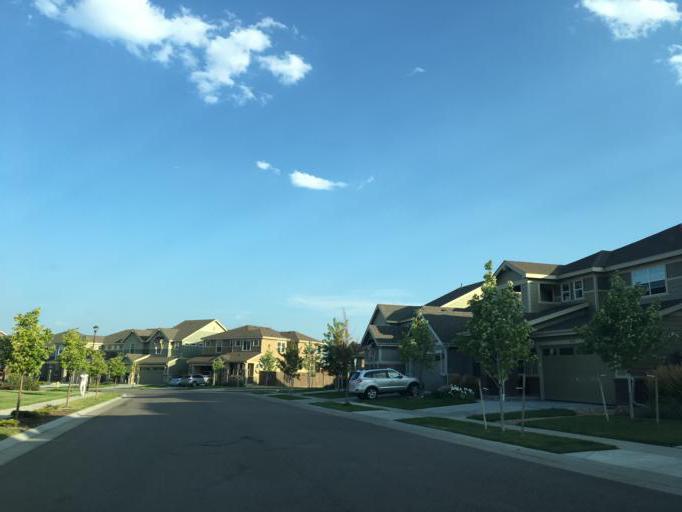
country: US
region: Colorado
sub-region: Jefferson County
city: Applewood
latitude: 39.7867
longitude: -105.1716
